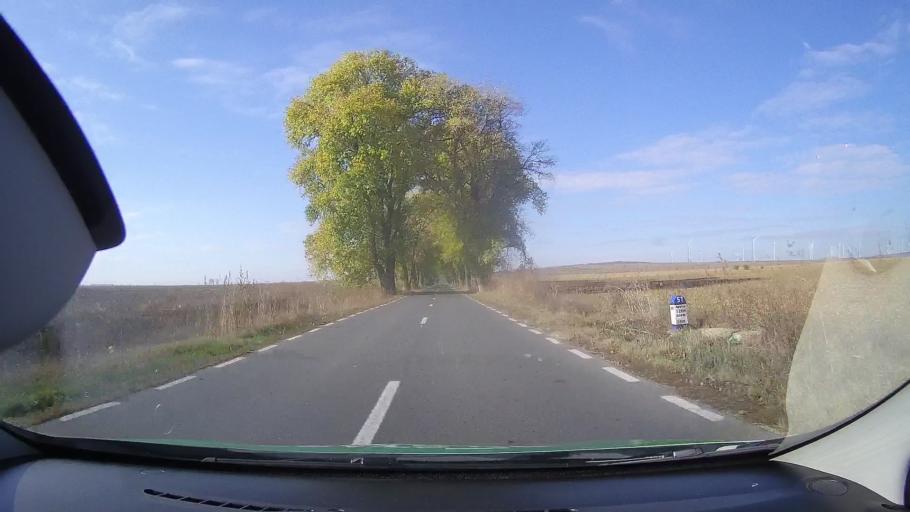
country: RO
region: Tulcea
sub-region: Comuna Valea Nucarilor
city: Iazurile
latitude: 45.0269
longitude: 29.0072
